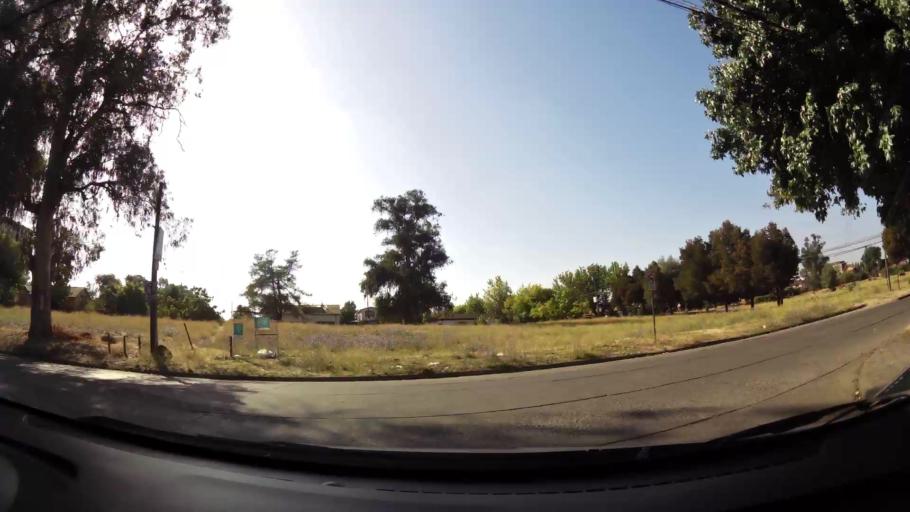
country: CL
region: Maule
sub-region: Provincia de Talca
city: Talca
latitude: -35.4164
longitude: -71.6680
